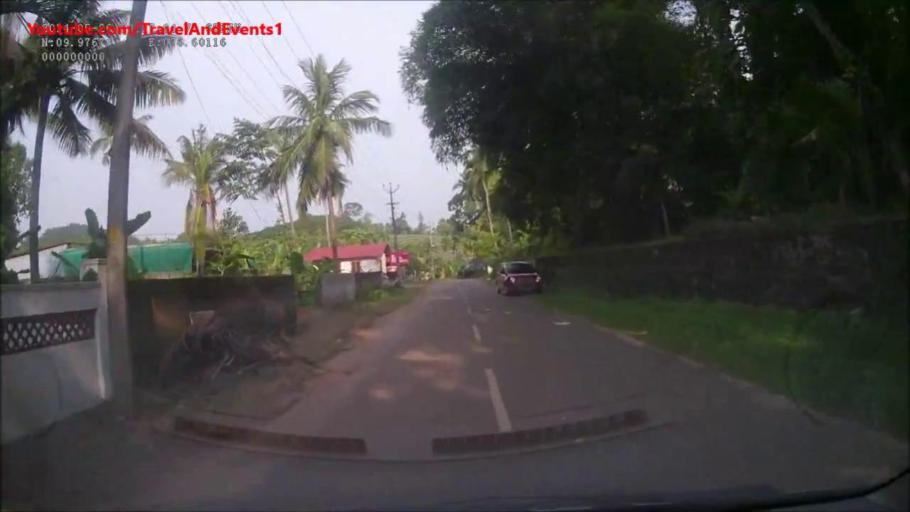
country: IN
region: Kerala
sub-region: Ernakulam
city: Muvattupula
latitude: 9.9713
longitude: 76.6072
